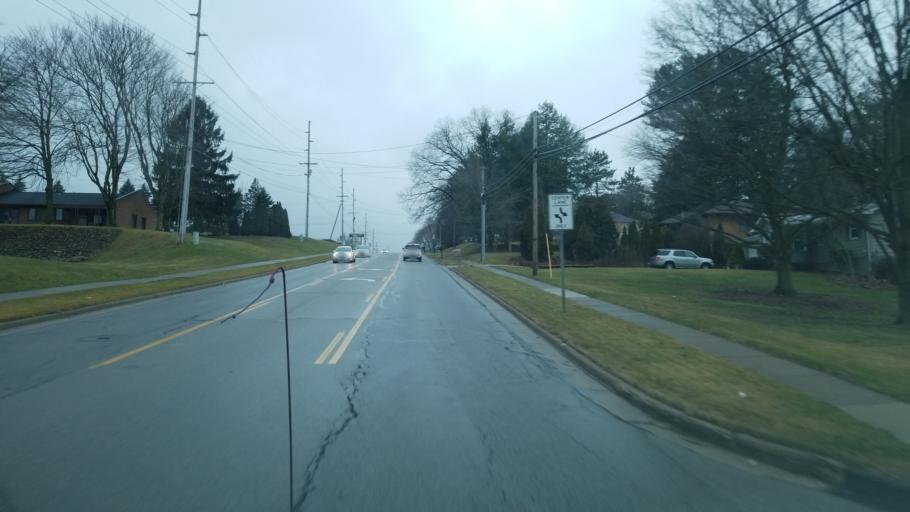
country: US
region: Ohio
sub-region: Wayne County
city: Wooster
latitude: 40.8249
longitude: -81.9283
